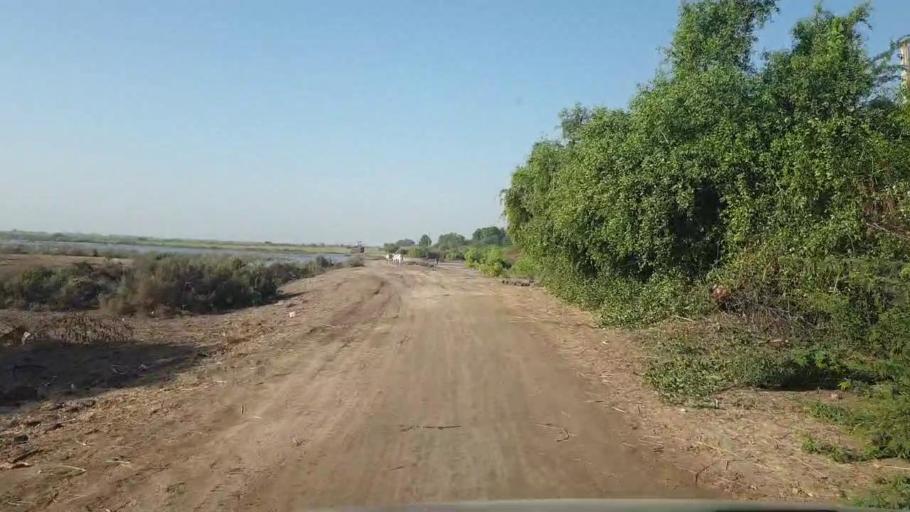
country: PK
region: Sindh
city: Badin
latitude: 24.7143
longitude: 68.7889
